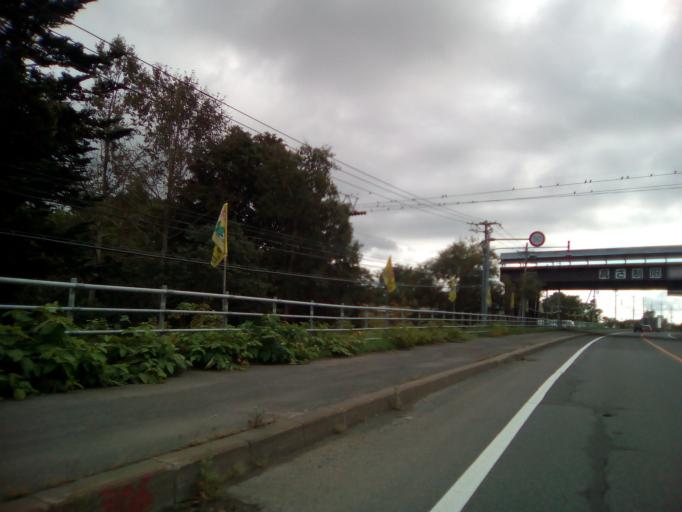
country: JP
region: Hokkaido
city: Niseko Town
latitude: 42.7491
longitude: 140.9015
